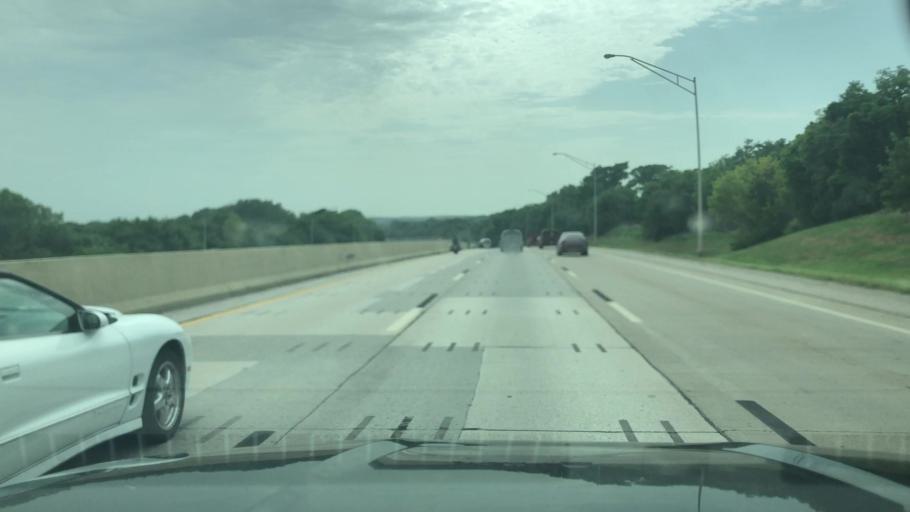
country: US
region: Oklahoma
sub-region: Tulsa County
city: Tulsa
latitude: 36.1575
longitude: -96.0304
